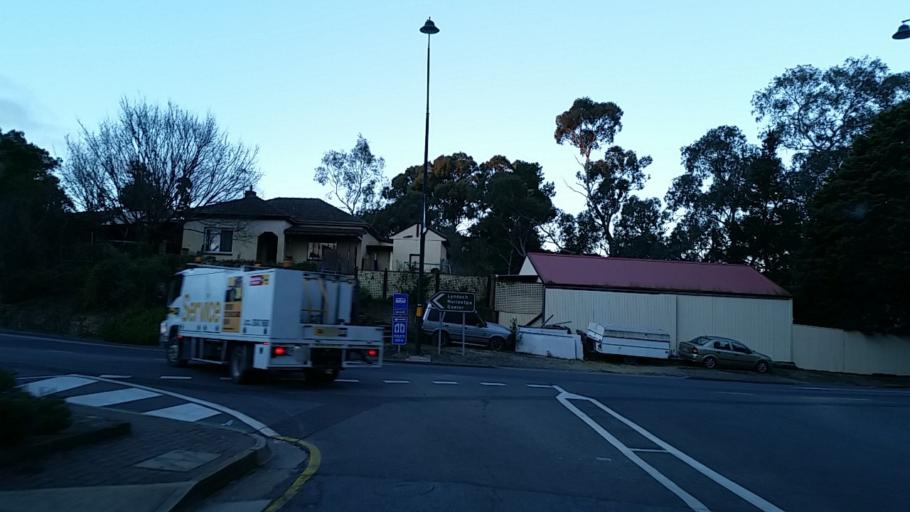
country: AU
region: South Australia
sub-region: Barossa
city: Williamstown
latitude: -34.6727
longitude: 138.8907
